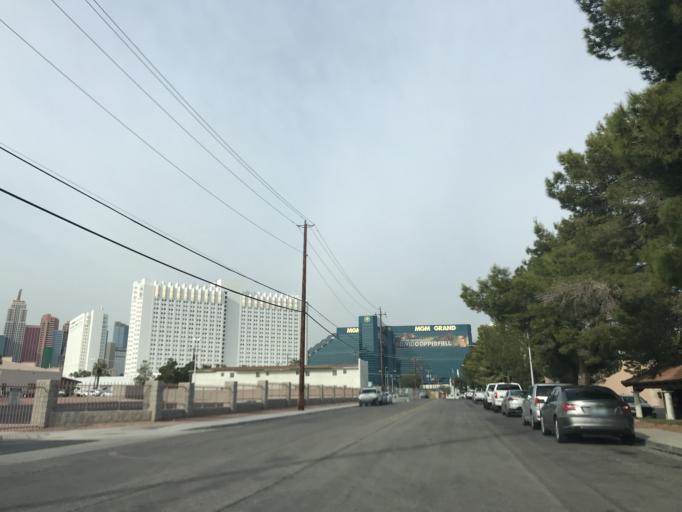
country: US
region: Nevada
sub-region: Clark County
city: Paradise
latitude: 36.0955
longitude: -115.1683
